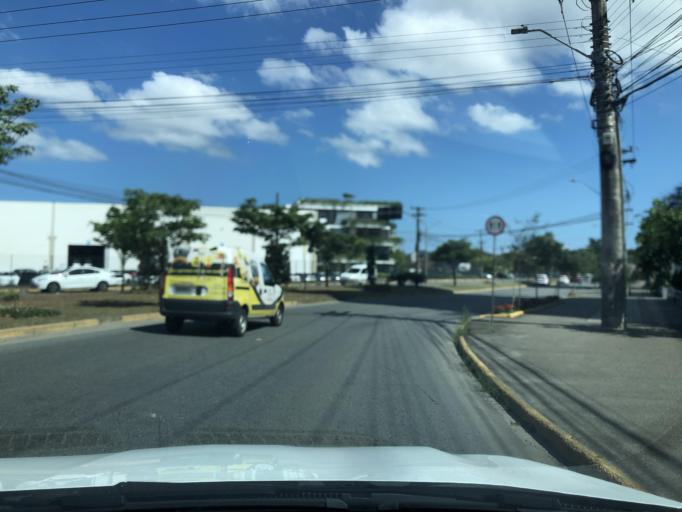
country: BR
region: Santa Catarina
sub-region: Joinville
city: Joinville
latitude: -26.2512
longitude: -48.8530
